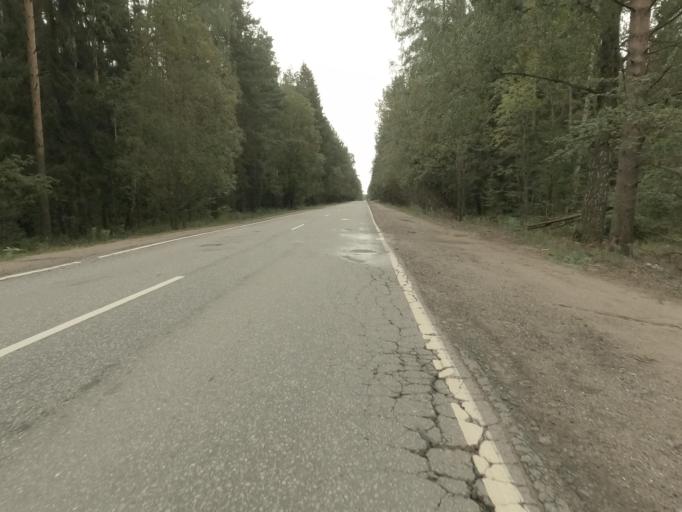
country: RU
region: Leningrad
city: Koltushi
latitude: 59.8949
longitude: 30.7493
